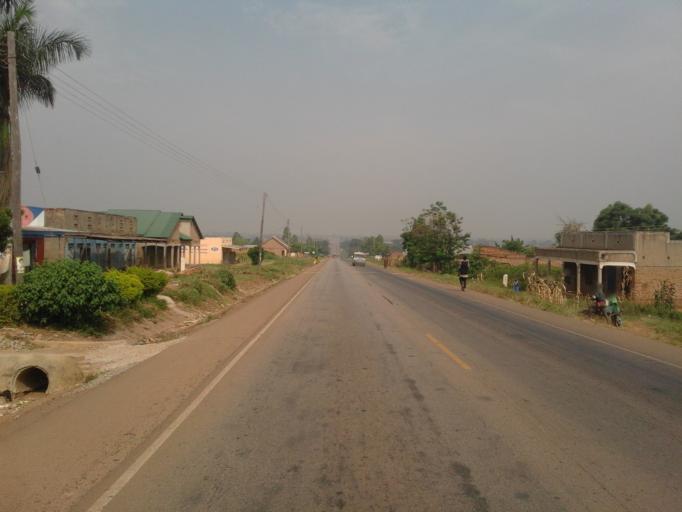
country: UG
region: Eastern Region
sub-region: Bugiri District
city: Bugiri
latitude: 0.5577
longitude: 33.7625
